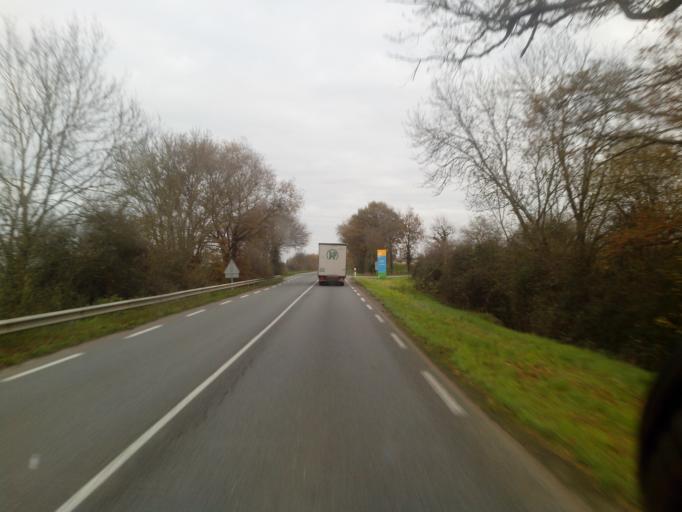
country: FR
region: Poitou-Charentes
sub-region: Departement des Deux-Sevres
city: Chatillon-sur-Thouet
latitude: 46.6480
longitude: -0.1999
